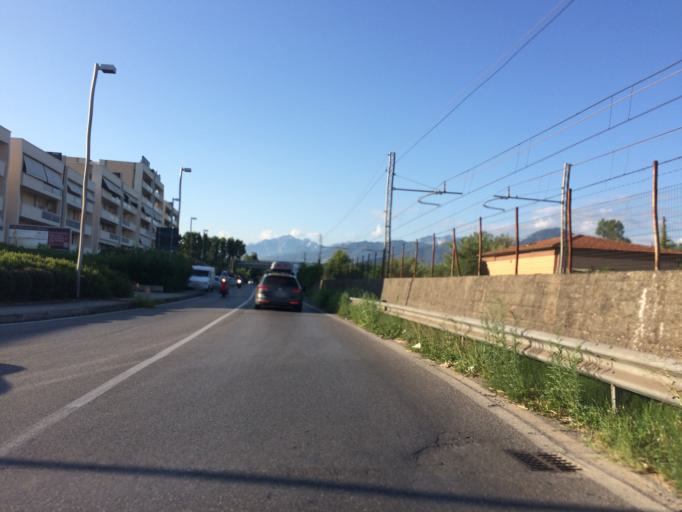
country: IT
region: Tuscany
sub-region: Provincia di Lucca
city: Viareggio
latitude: 43.8863
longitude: 10.2506
